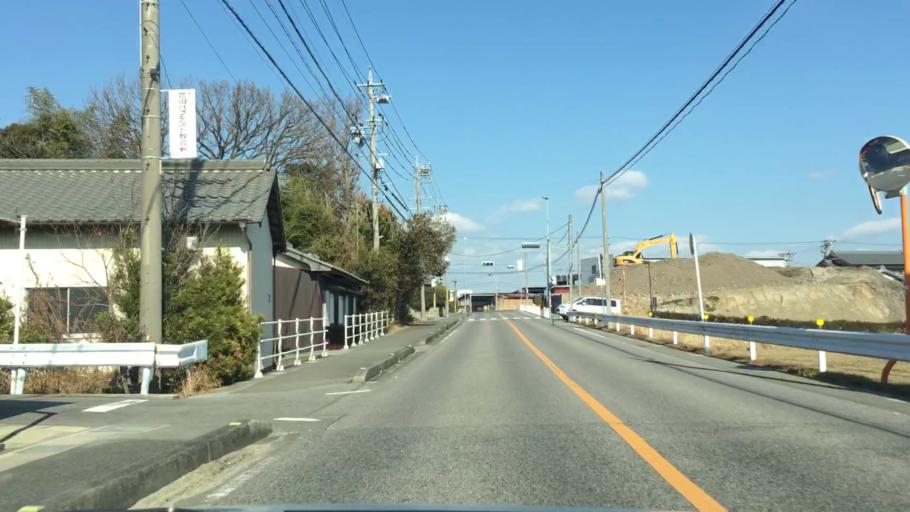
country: JP
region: Aichi
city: Anjo
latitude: 35.0059
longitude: 137.1193
